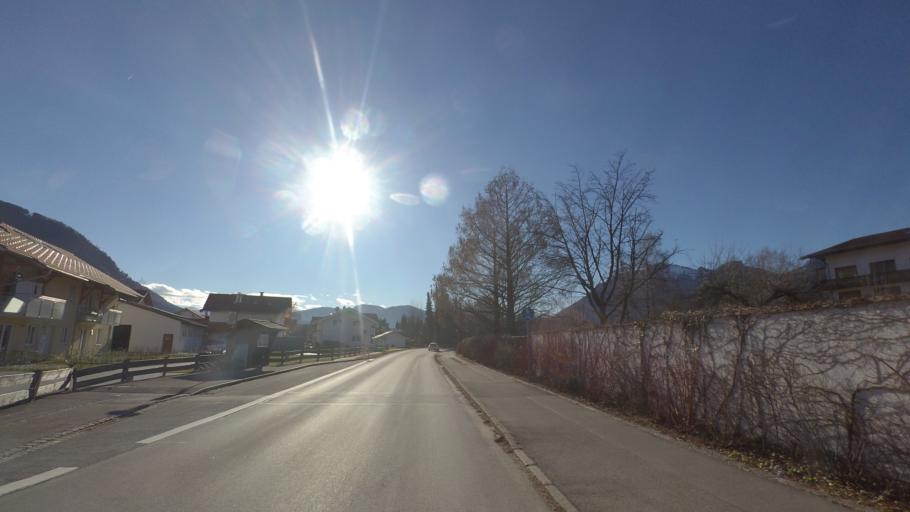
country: DE
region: Bavaria
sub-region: Upper Bavaria
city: Grassau
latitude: 47.7856
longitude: 12.4660
